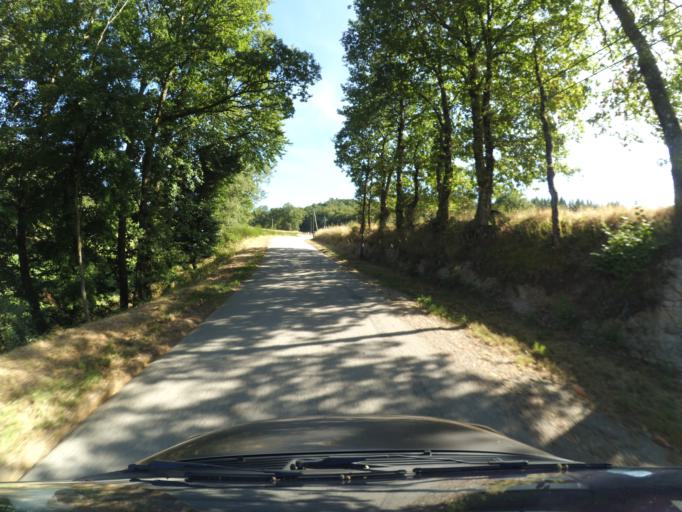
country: FR
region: Limousin
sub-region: Departement de la Correze
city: Bugeat
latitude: 45.7030
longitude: 1.8757
